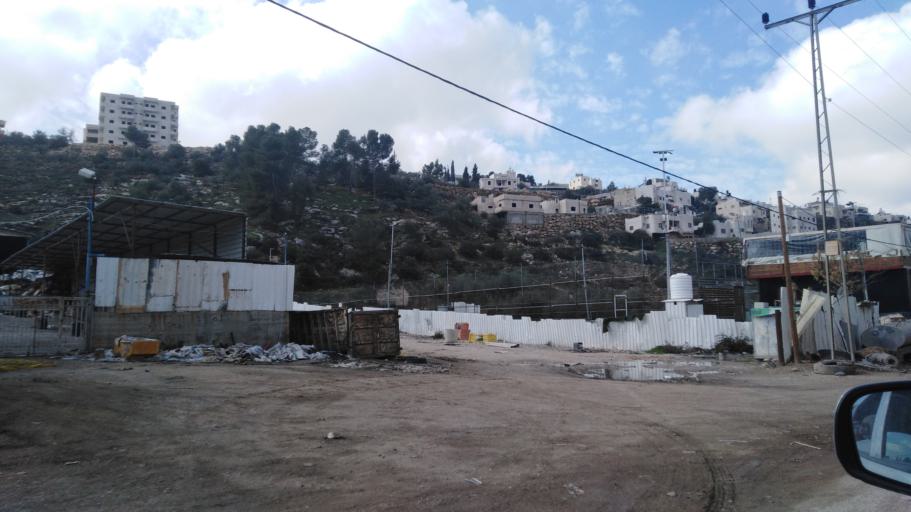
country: PS
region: West Bank
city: Idhna
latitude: 31.5568
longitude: 34.9859
